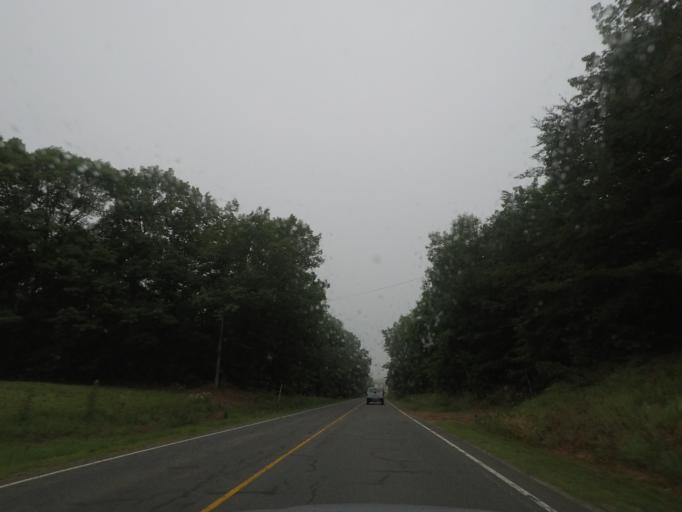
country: US
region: Virginia
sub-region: Buckingham County
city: Buckingham
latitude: 37.5138
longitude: -78.4915
